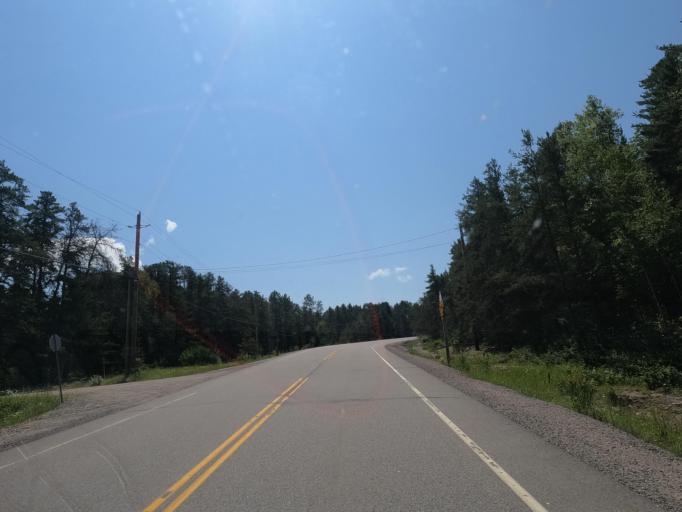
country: CA
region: Ontario
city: Dryden
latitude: 49.8565
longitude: -93.3636
